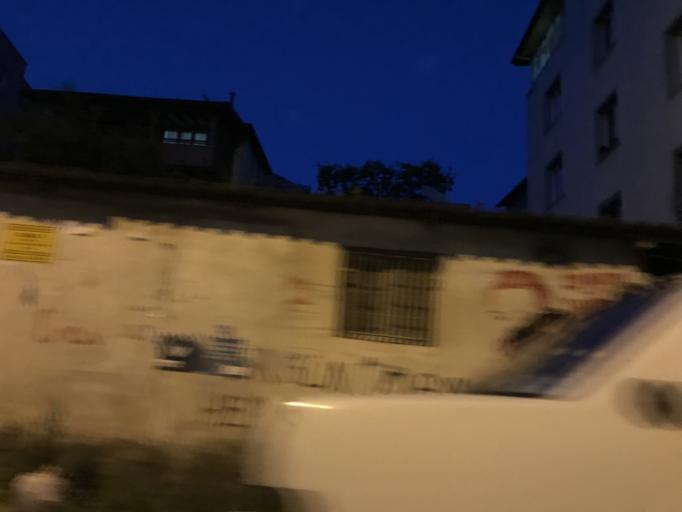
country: TR
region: Hatay
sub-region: Antakya Ilcesi
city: Antakya
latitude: 36.1967
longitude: 36.1478
